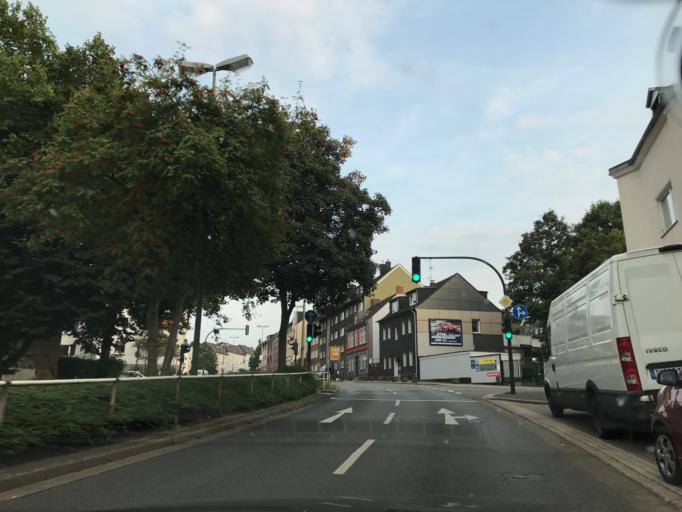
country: DE
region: North Rhine-Westphalia
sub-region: Regierungsbezirk Dusseldorf
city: Essen
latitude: 51.4457
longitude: 6.9688
